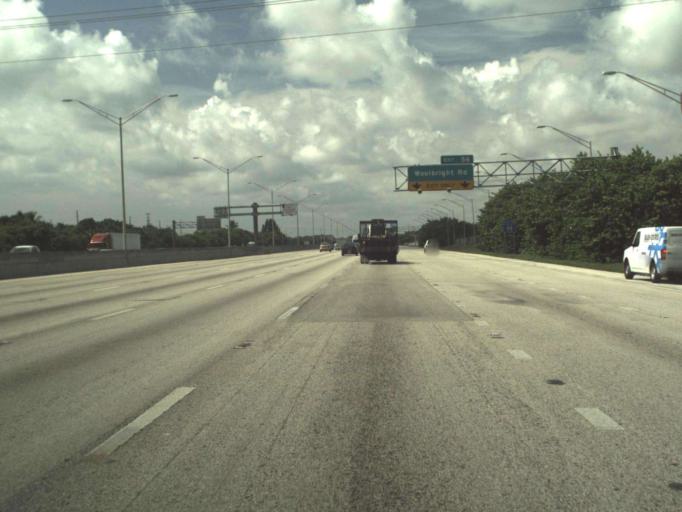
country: US
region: Florida
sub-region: Palm Beach County
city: Boynton Beach
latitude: 26.5238
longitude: -80.0730
